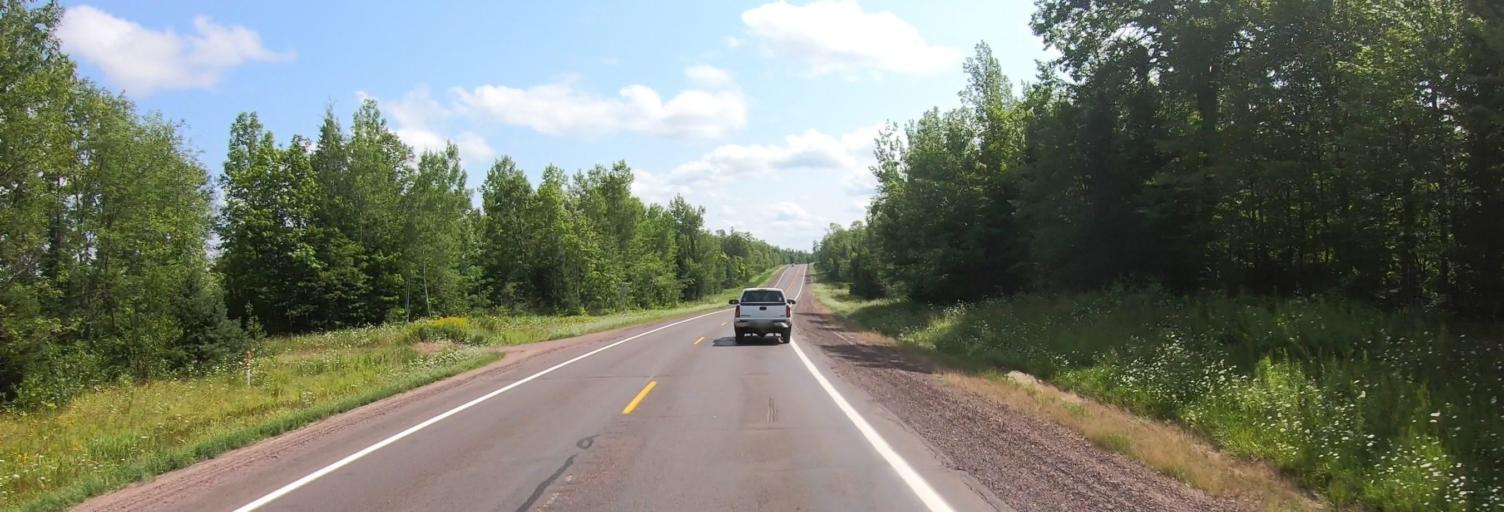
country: US
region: Michigan
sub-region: Ontonagon County
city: Ontonagon
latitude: 46.8161
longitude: -88.9959
